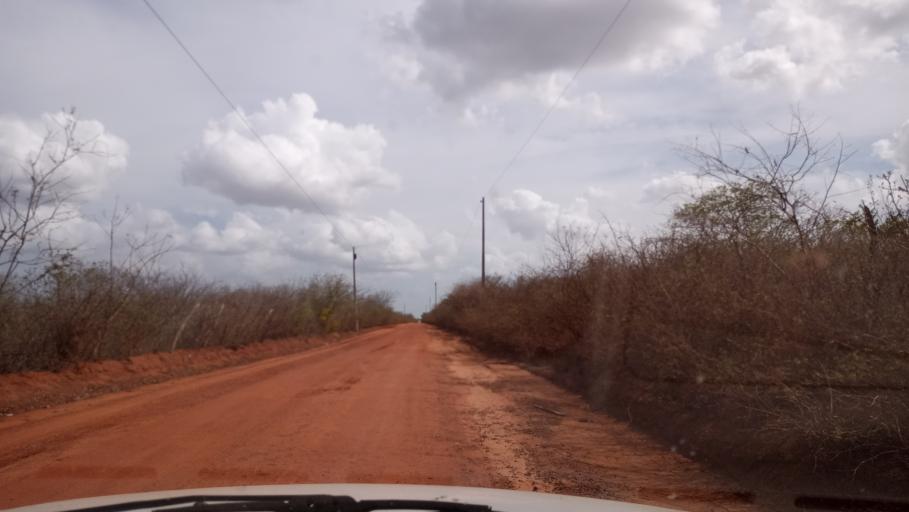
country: BR
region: Rio Grande do Norte
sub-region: Joao Camara
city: Joao Camara
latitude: -5.4767
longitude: -35.8275
